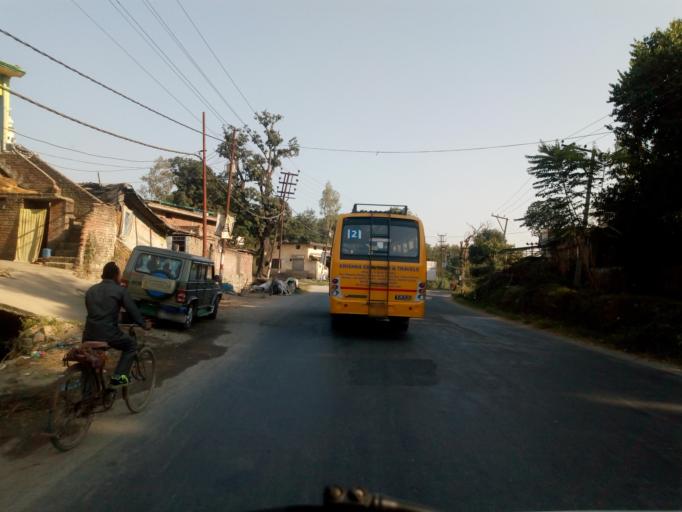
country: IN
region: Uttarakhand
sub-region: Dehradun
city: Harbatpur
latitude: 30.4032
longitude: 77.7959
